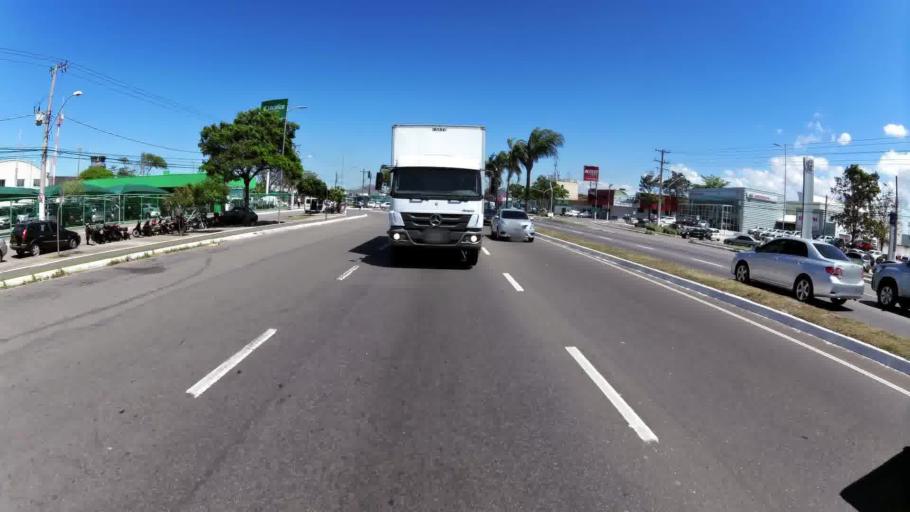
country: BR
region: Espirito Santo
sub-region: Vila Velha
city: Vila Velha
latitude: -20.2554
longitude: -40.2895
